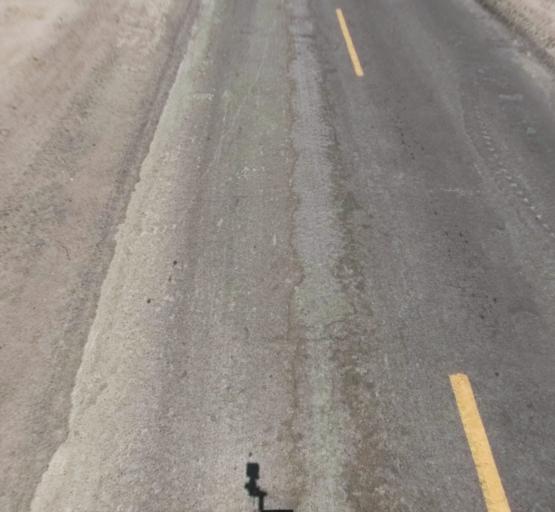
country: US
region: California
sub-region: Madera County
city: Parkwood
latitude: 36.8566
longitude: -120.0922
